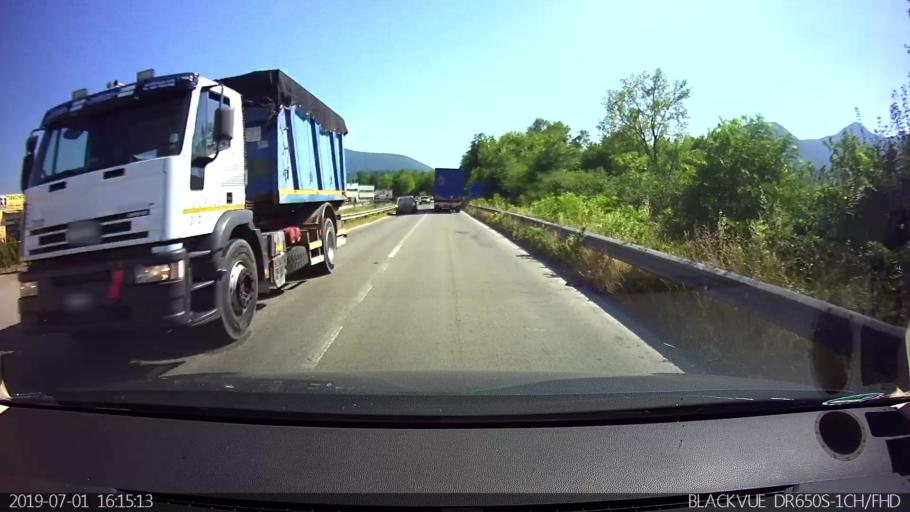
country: IT
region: Latium
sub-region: Provincia di Frosinone
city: Ceccano
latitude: 41.5947
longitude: 13.2915
